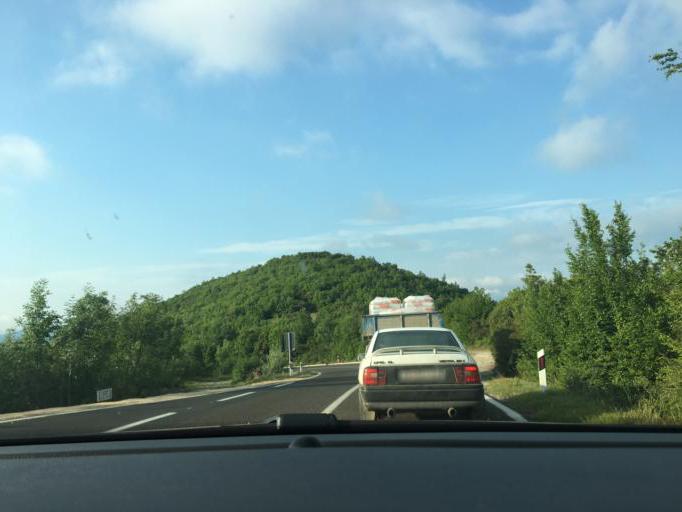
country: MK
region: Valandovo
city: Valandovo
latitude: 41.3375
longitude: 22.5886
